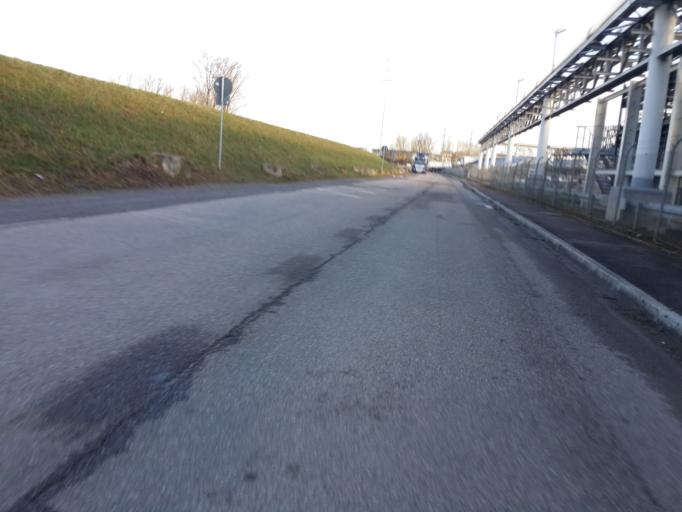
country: DE
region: Baden-Wuerttemberg
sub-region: Regierungsbezirk Stuttgart
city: Untereisesheim
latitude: 49.2048
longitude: 9.2178
